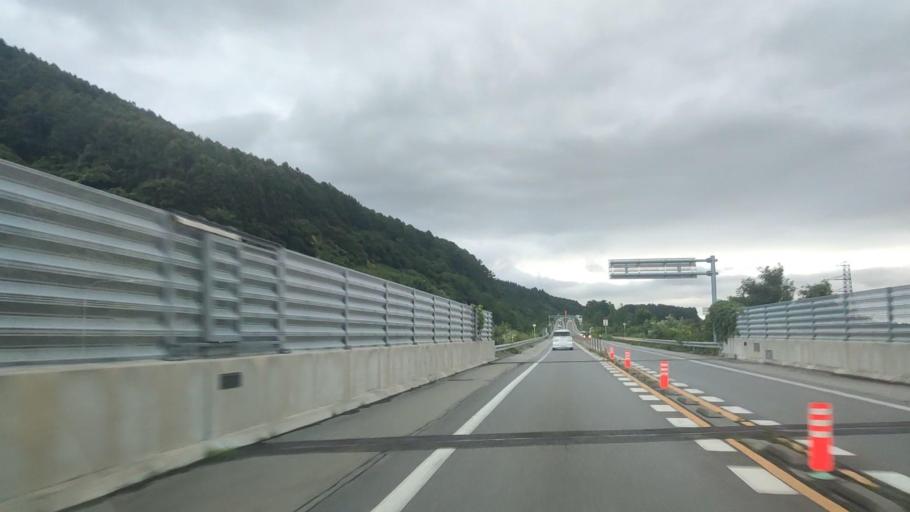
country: JP
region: Hokkaido
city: Nanae
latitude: 41.9135
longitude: 140.6910
